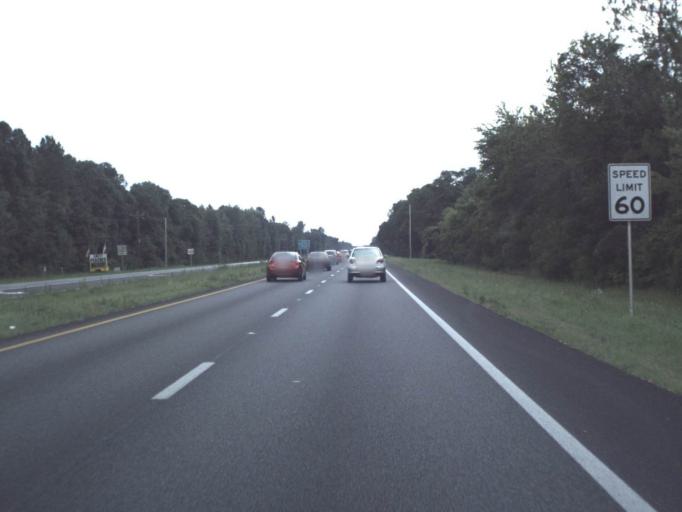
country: US
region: Florida
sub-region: Duval County
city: Baldwin
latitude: 30.1852
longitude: -82.0209
